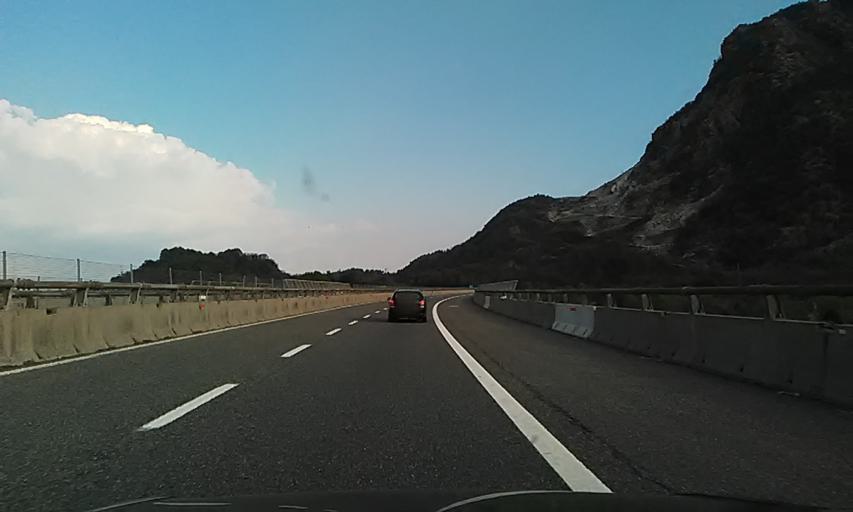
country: IT
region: Piedmont
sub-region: Provincia Verbano-Cusio-Ossola
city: Mergozzo
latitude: 45.9301
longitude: 8.4707
